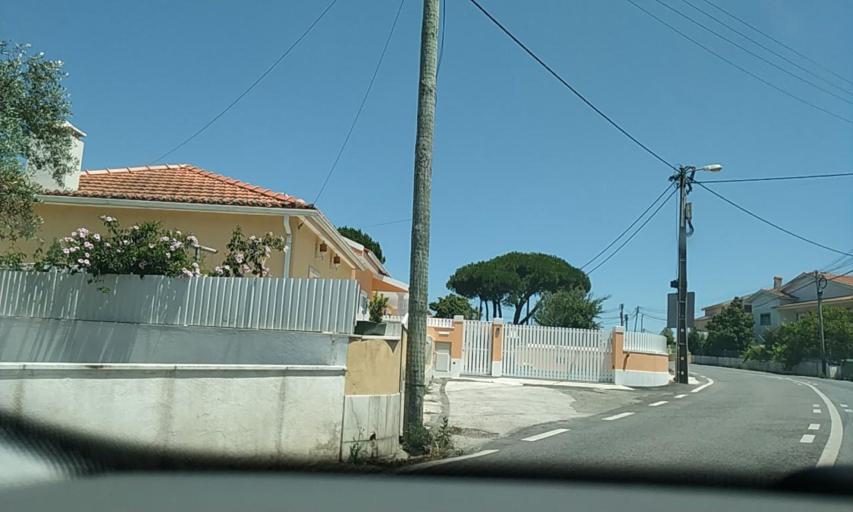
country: PT
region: Lisbon
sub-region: Sintra
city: Almargem
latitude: 38.8784
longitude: -9.2755
